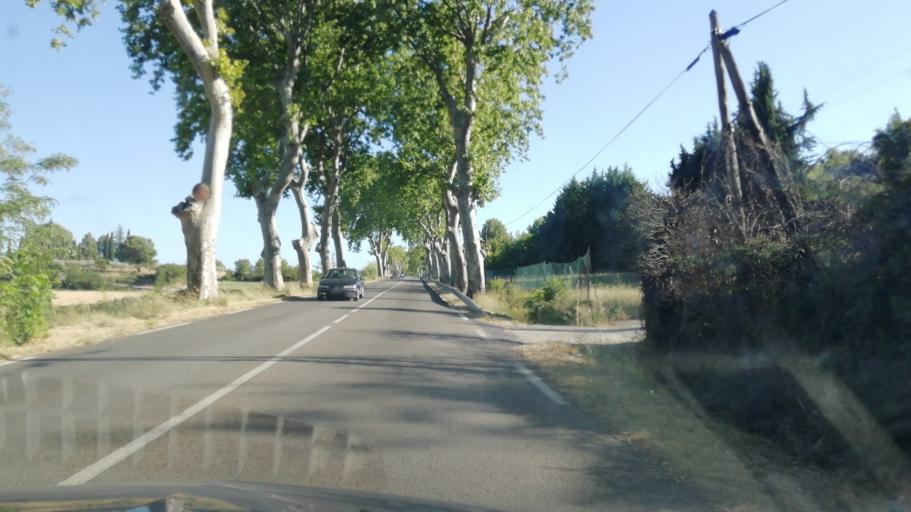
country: FR
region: Languedoc-Roussillon
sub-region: Departement de l'Herault
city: Nebian
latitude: 43.6164
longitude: 3.4367
